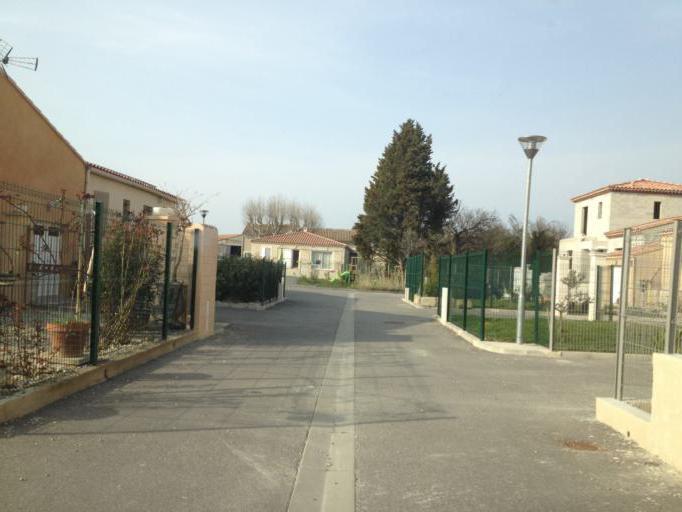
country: FR
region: Provence-Alpes-Cote d'Azur
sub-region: Departement du Vaucluse
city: Courthezon
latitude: 44.0885
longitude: 4.8902
